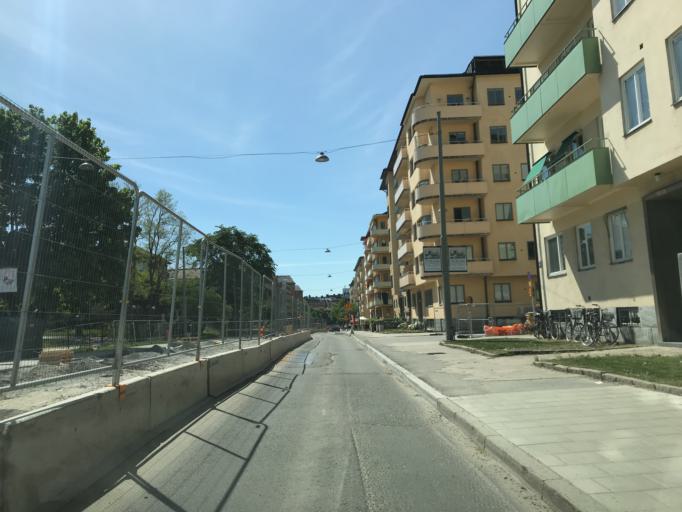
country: SE
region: Stockholm
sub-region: Stockholms Kommun
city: OEstermalm
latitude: 59.3429
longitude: 18.0988
